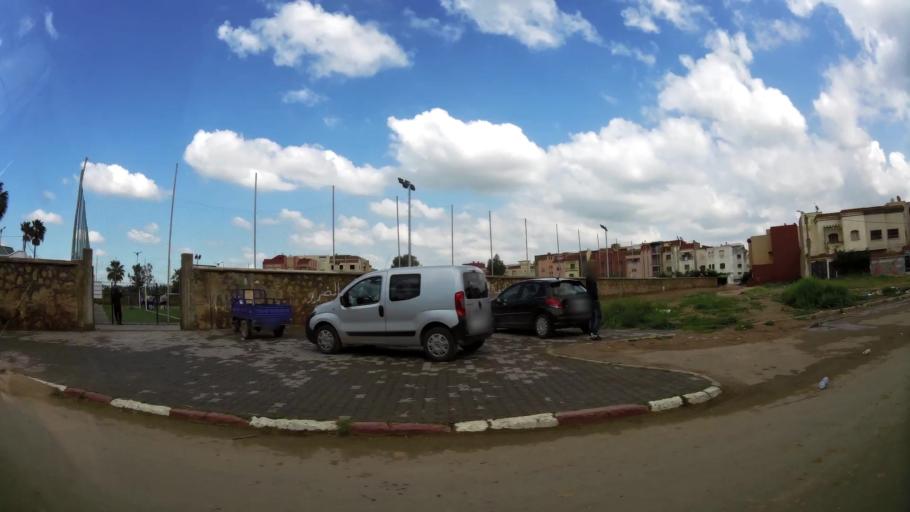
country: MA
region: Grand Casablanca
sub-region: Mediouna
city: Mediouna
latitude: 33.3726
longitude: -7.5309
